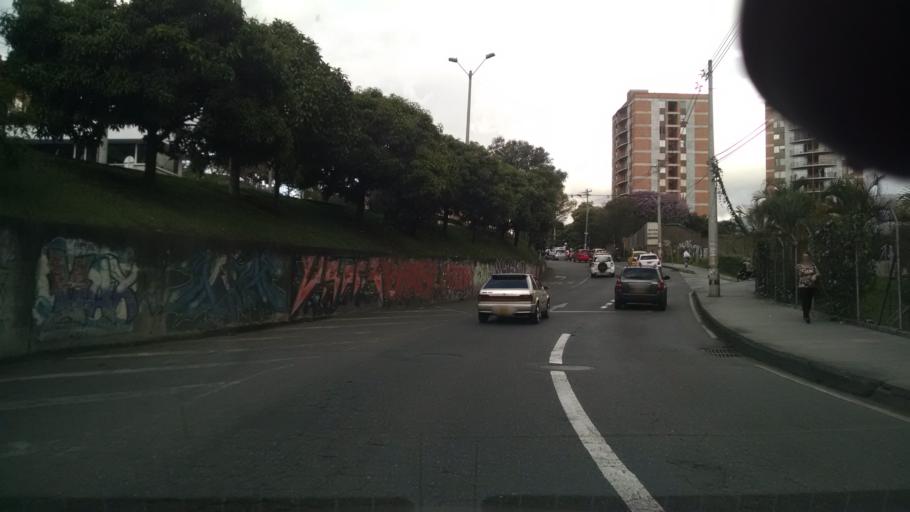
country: CO
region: Antioquia
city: Medellin
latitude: 6.2784
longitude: -75.5885
